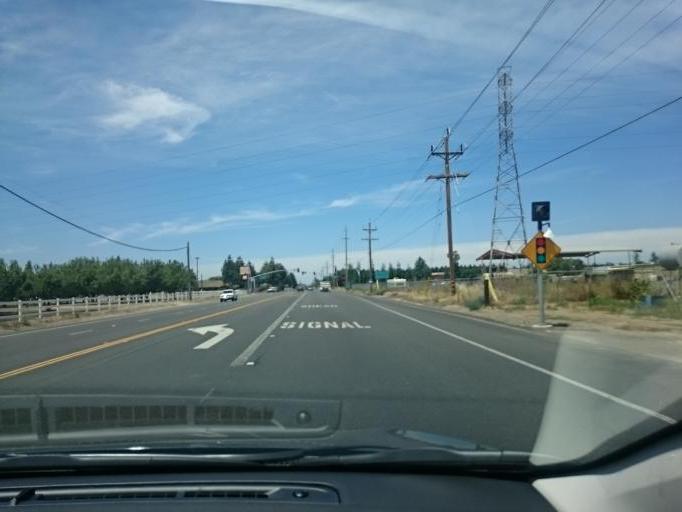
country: US
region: California
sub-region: Stanislaus County
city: Hughson
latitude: 37.6387
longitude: -120.8456
